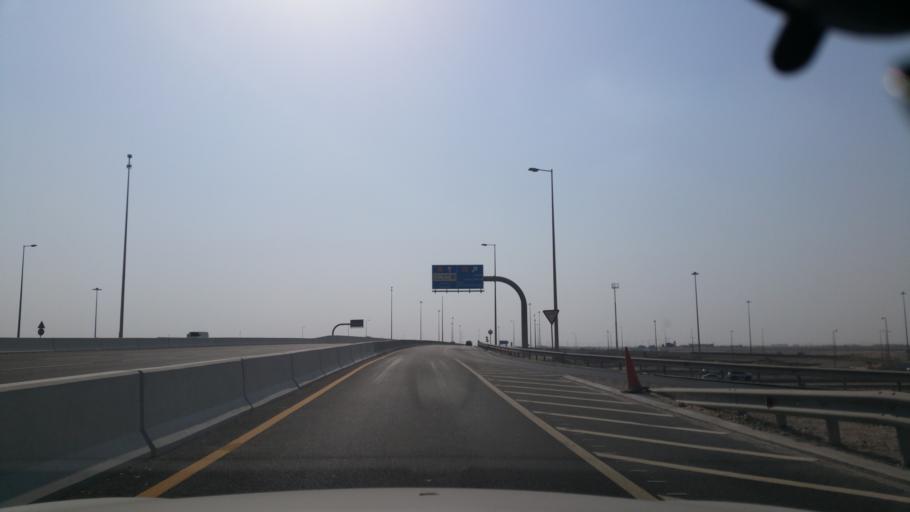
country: QA
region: Baladiyat Umm Salal
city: Umm Salal `Ali
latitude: 25.4488
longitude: 51.4118
